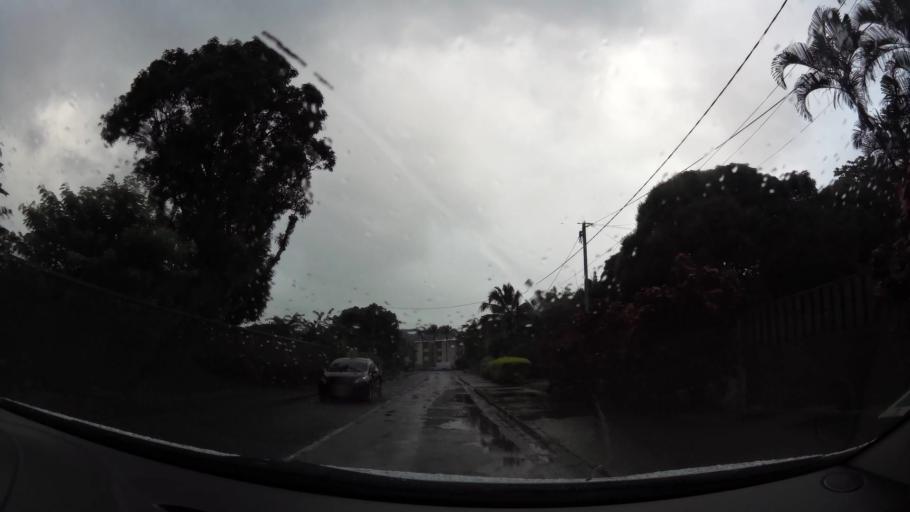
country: RE
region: Reunion
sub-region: Reunion
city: Saint-Benoit
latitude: -21.0358
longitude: 55.7086
